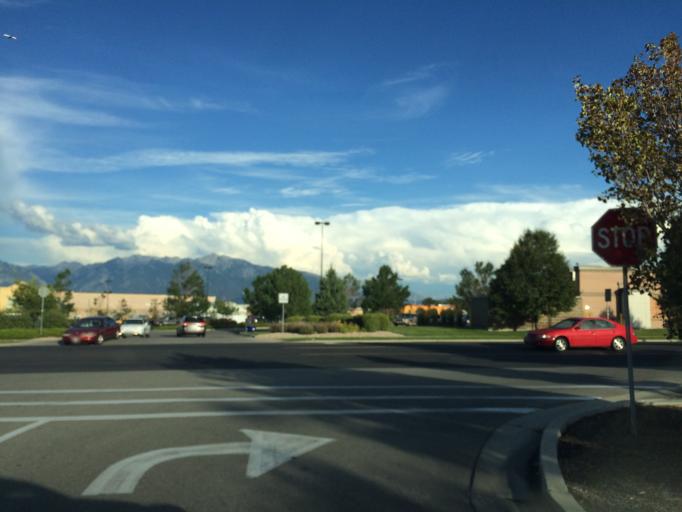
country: US
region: Utah
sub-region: Salt Lake County
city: West Jordan
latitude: 40.6115
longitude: -111.9810
